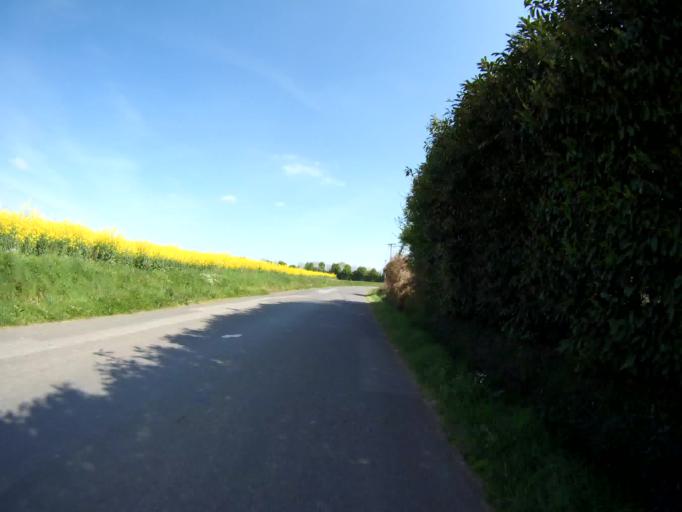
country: FR
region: Brittany
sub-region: Departement d'Ille-et-Vilaine
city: Saint-Erblon
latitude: 48.0218
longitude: -1.6339
